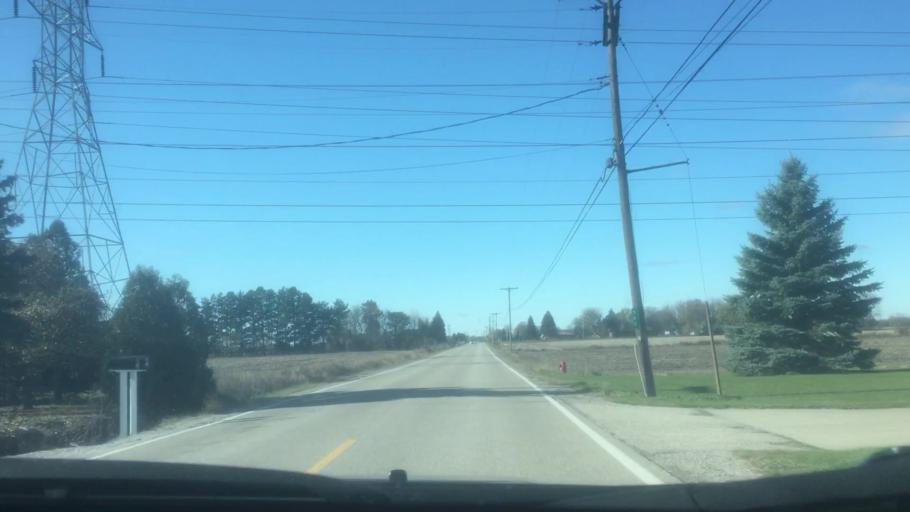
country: US
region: Michigan
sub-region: Bay County
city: Essexville
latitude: 43.5798
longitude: -83.7940
